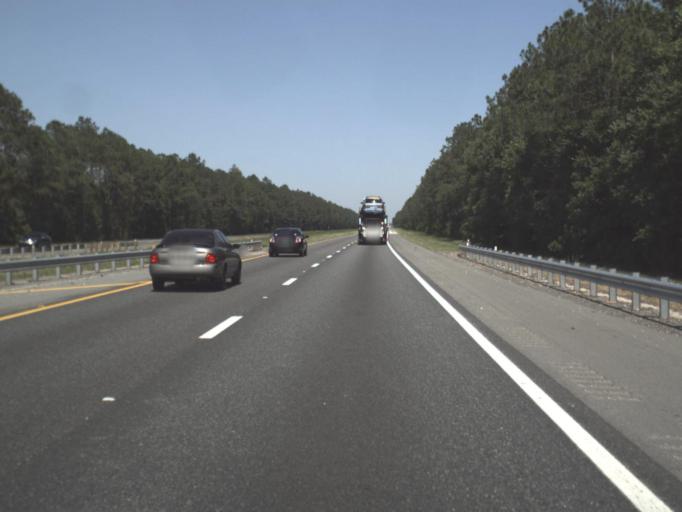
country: US
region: Florida
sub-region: Duval County
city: Baldwin
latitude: 30.2860
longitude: -82.0210
